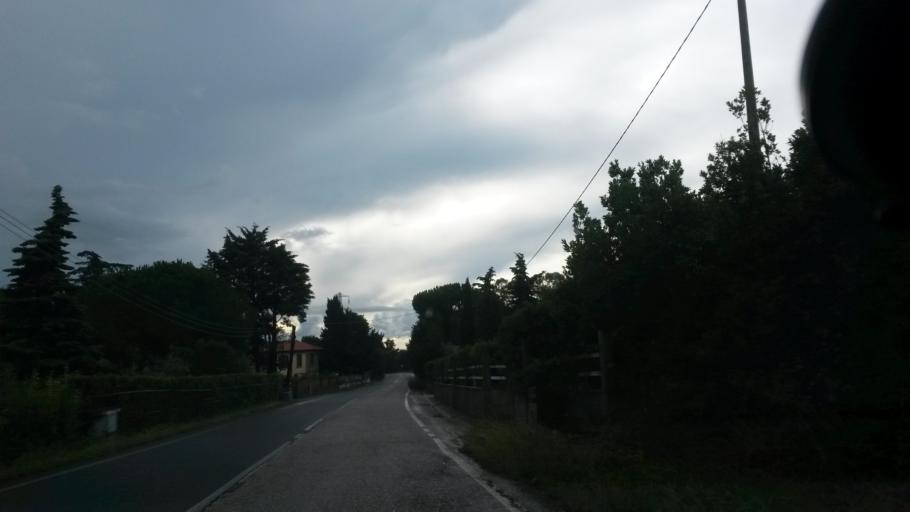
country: IT
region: Tuscany
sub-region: Provincia di Livorno
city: Rosignano Marittimo
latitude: 43.4143
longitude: 10.4515
